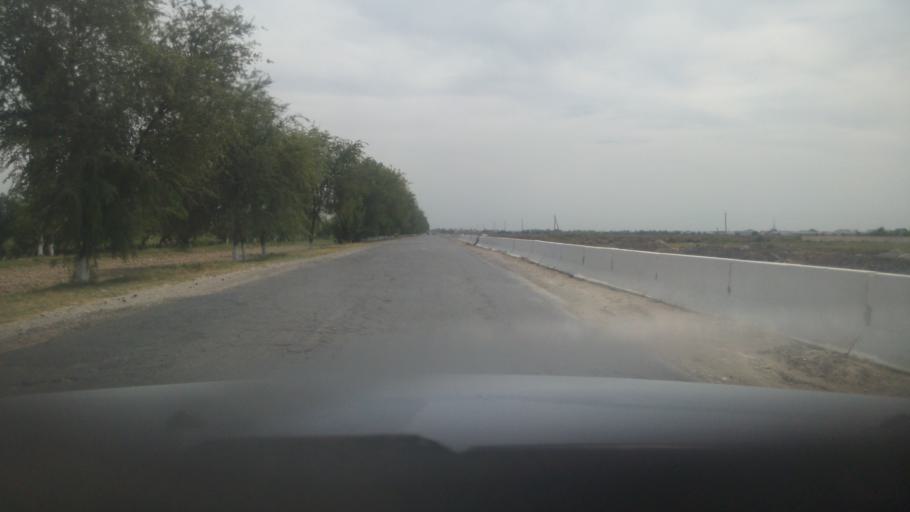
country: UZ
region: Sirdaryo
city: Guliston
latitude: 40.5164
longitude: 68.7936
